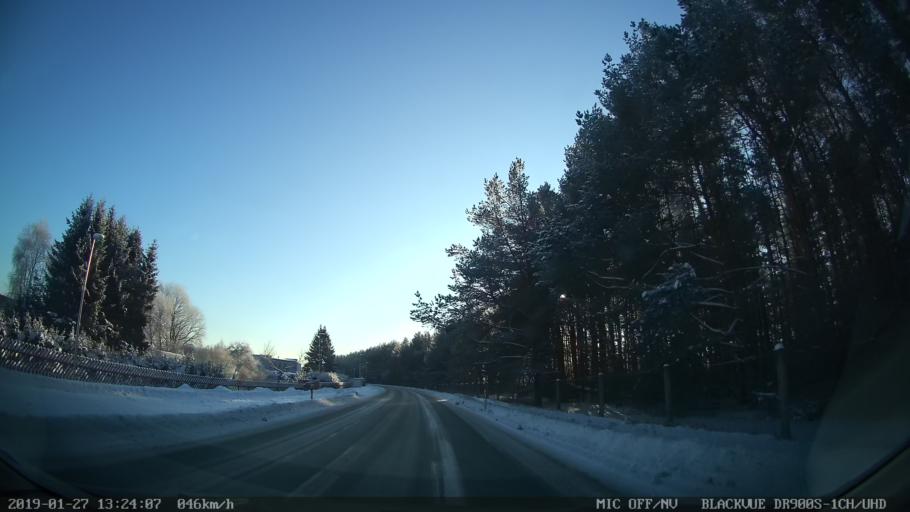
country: EE
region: Harju
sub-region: Tallinna linn
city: Tallinn
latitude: 59.4017
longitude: 24.7901
